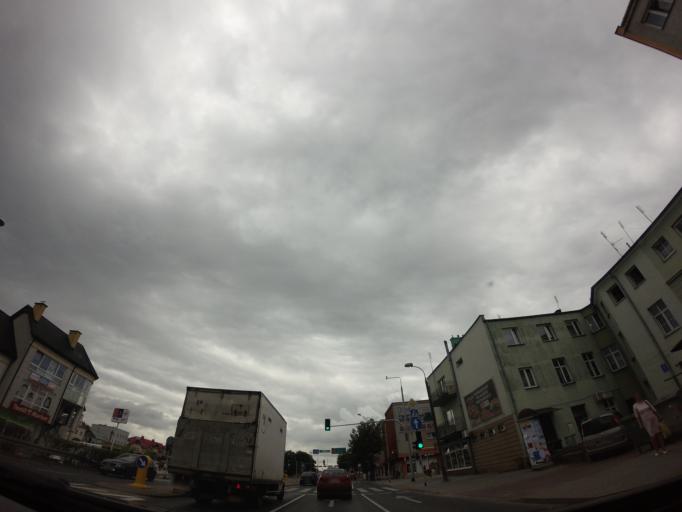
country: PL
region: Masovian Voivodeship
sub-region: Powiat ciechanowski
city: Ciechanow
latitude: 52.8816
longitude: 20.6175
